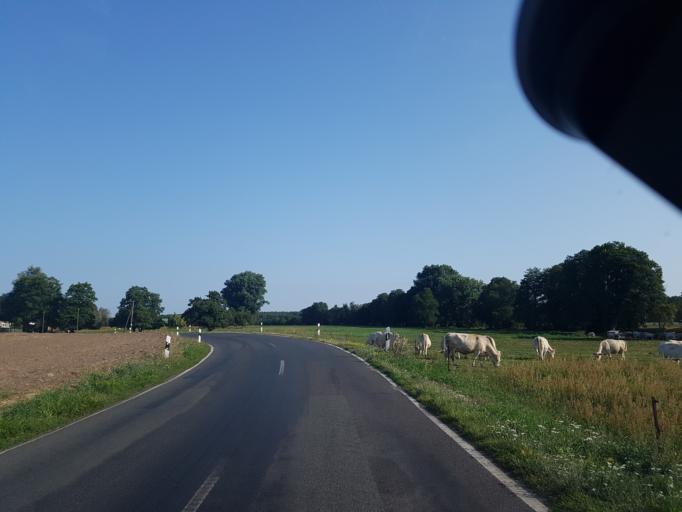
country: DE
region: Brandenburg
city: Niemegk
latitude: 52.1576
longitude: 12.6911
